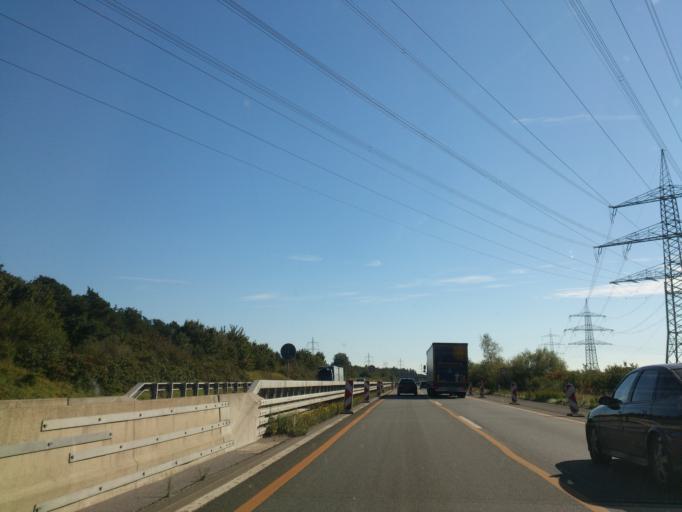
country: DE
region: North Rhine-Westphalia
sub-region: Regierungsbezirk Detmold
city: Hovelhof
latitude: 51.8624
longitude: 8.6620
